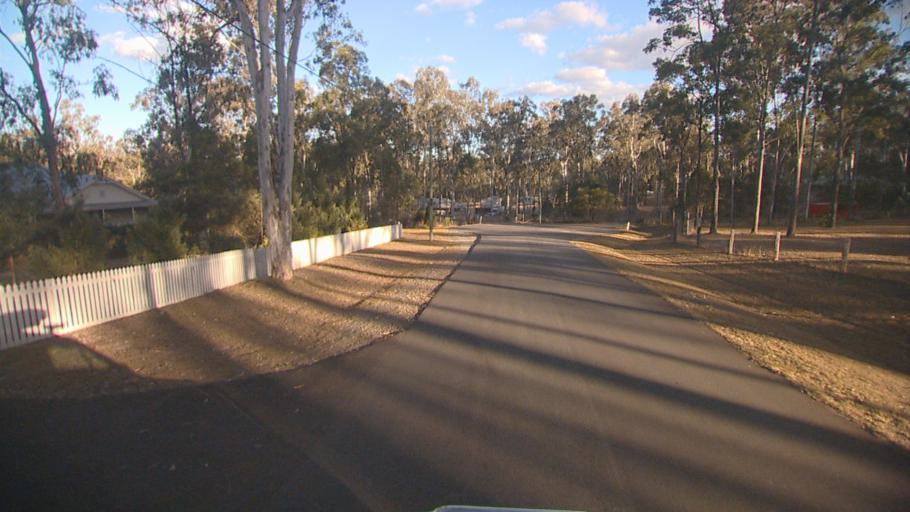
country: AU
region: Queensland
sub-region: Logan
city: Cedar Vale
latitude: -27.8567
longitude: 153.0980
